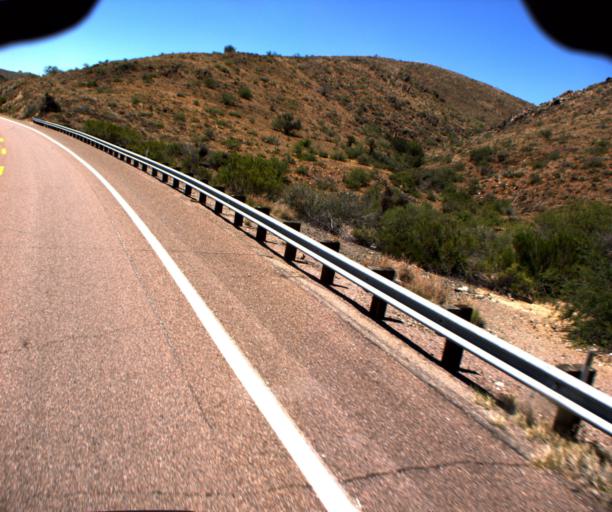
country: US
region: Arizona
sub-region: Yavapai County
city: Bagdad
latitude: 34.5557
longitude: -113.1556
